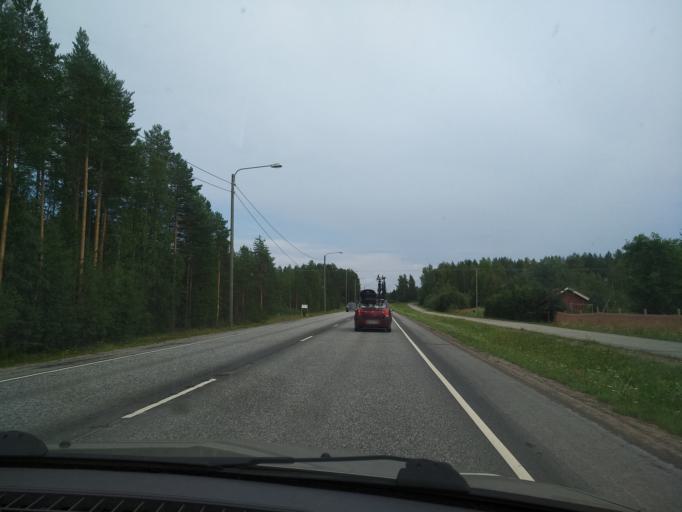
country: FI
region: Kainuu
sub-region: Kajaani
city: Paltamo
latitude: 64.4034
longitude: 27.8648
